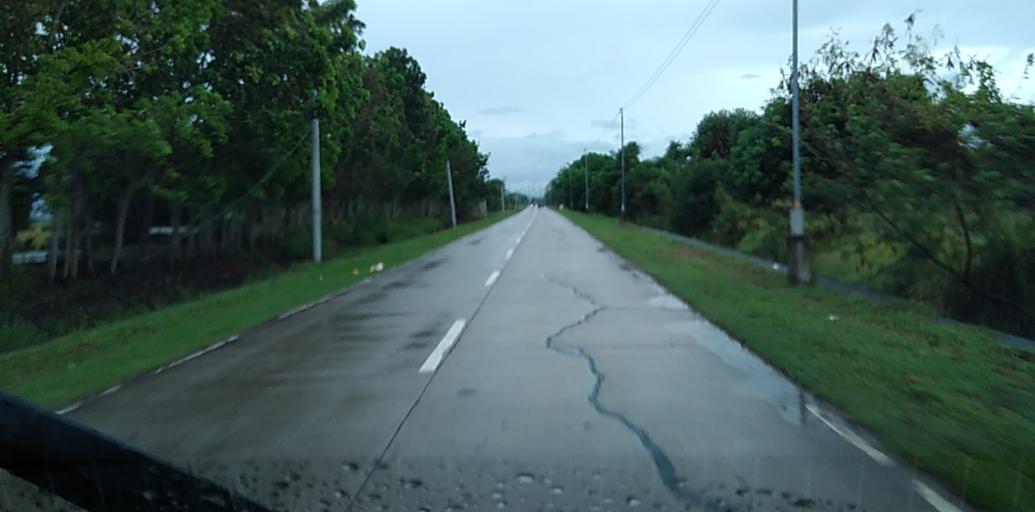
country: PH
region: Central Luzon
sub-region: Province of Pampanga
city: Salapungan
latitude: 15.1321
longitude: 120.8898
